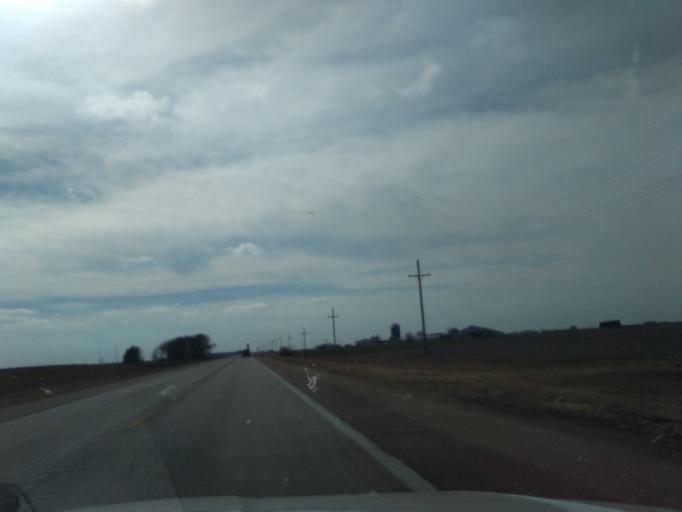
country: US
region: Nebraska
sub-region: Gage County
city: Beatrice
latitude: 40.2069
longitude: -96.9417
